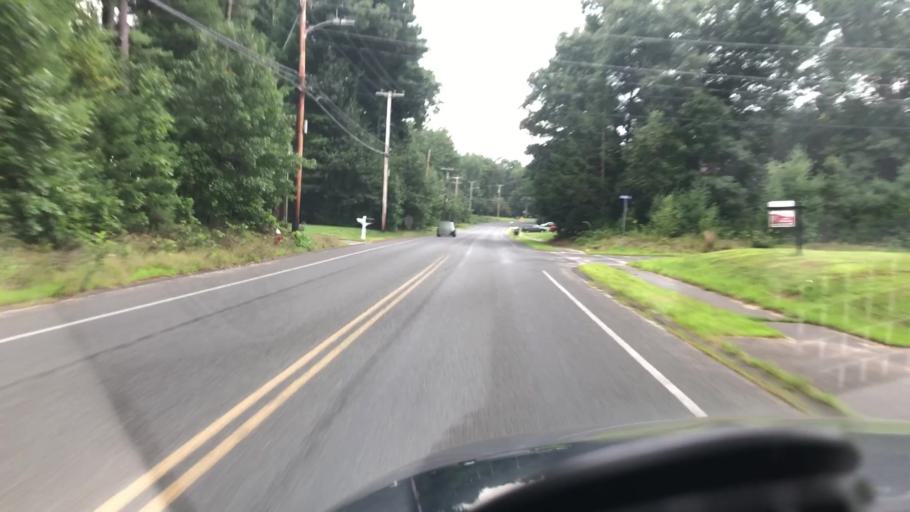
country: US
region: Massachusetts
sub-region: Hampshire County
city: Southampton
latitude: 42.1910
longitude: -72.6866
